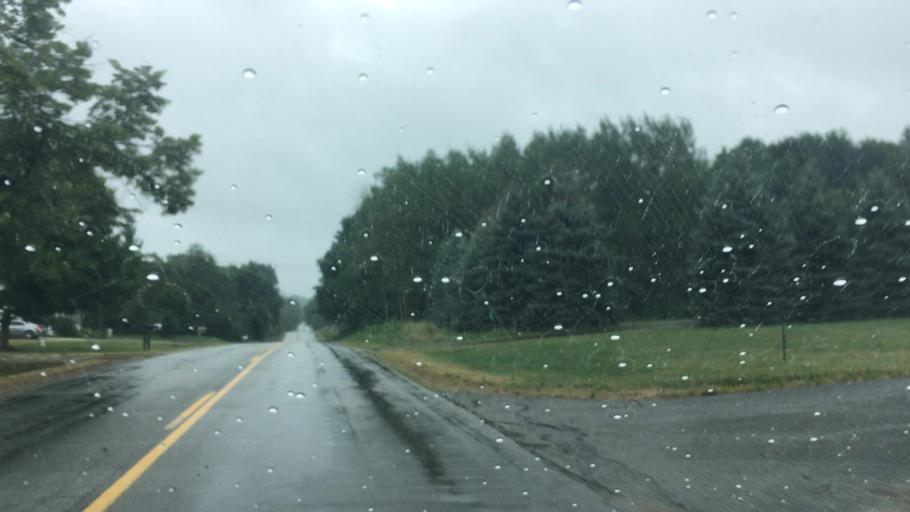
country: US
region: Michigan
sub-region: Ottawa County
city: Hudsonville
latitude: 42.8134
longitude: -85.8421
